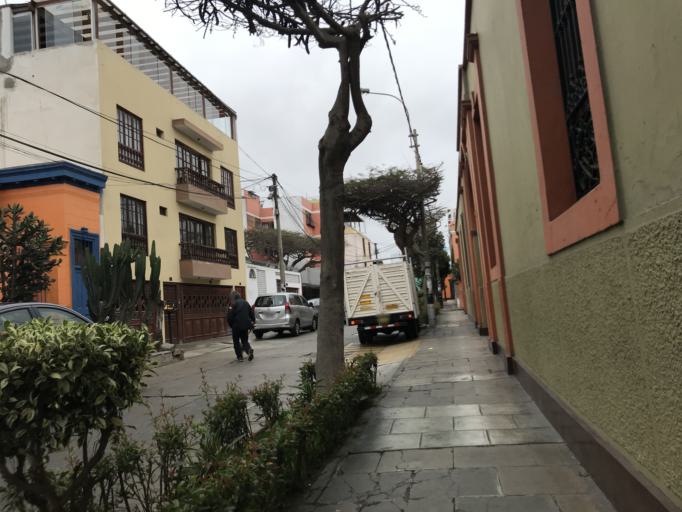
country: PE
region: Lima
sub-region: Lima
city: Surco
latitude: -12.1442
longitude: -77.0212
